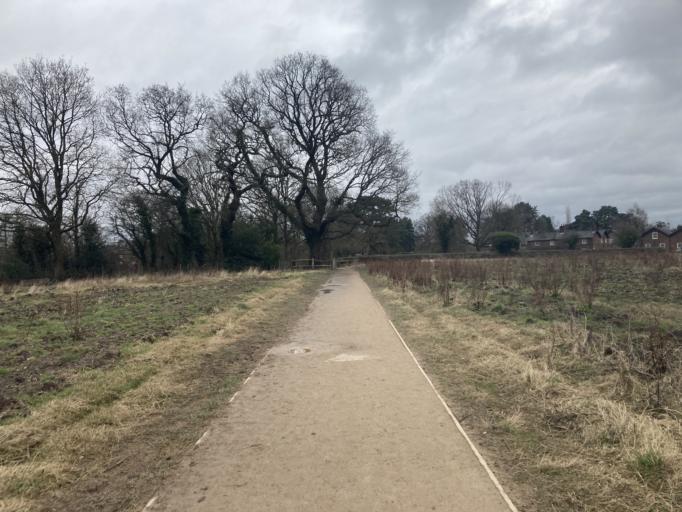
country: GB
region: England
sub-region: Cheshire East
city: Wilmslow
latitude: 53.3465
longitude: -2.2479
